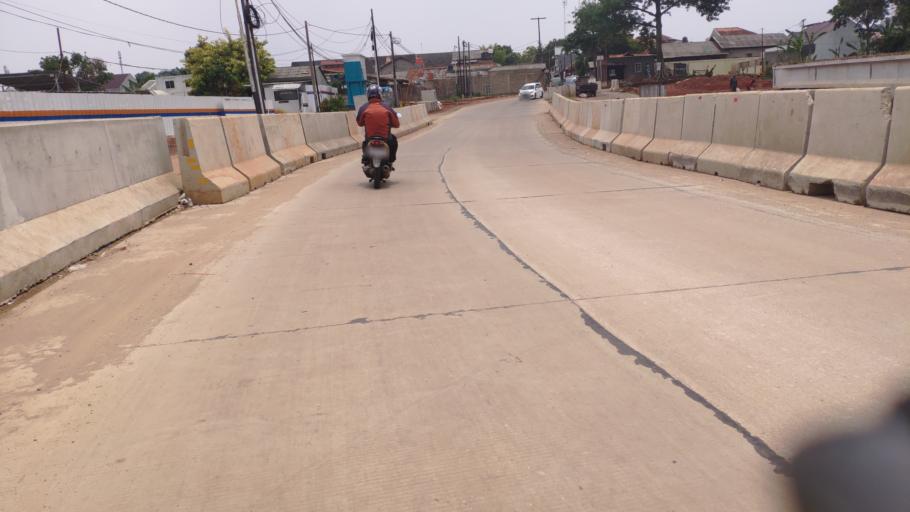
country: ID
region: West Java
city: Depok
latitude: -6.3436
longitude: 106.7992
